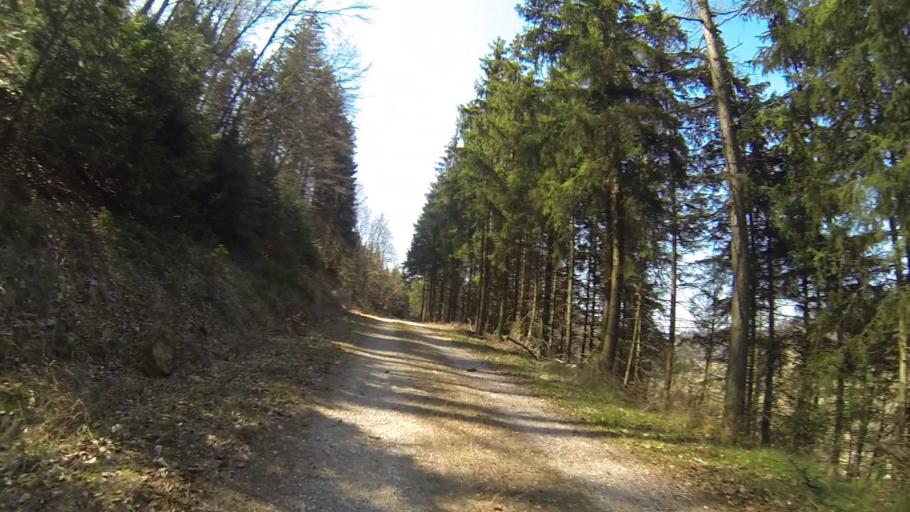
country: DE
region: Baden-Wuerttemberg
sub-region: Regierungsbezirk Stuttgart
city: Nattheim
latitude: 48.6943
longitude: 10.1994
